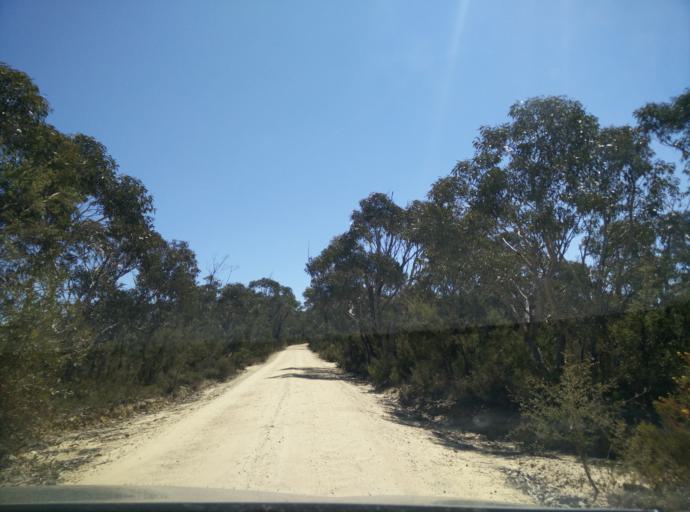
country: AU
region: New South Wales
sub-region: Blue Mountains Municipality
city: Blackheath
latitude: -33.5758
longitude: 150.2771
